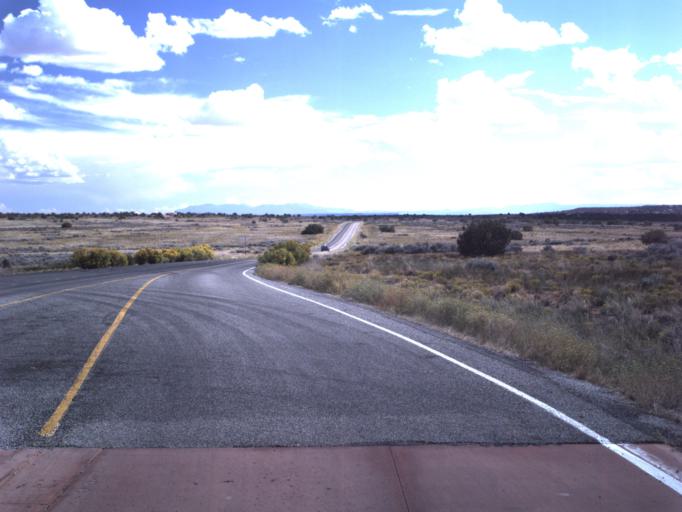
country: US
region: Utah
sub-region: Grand County
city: Moab
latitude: 38.5163
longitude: -109.7300
